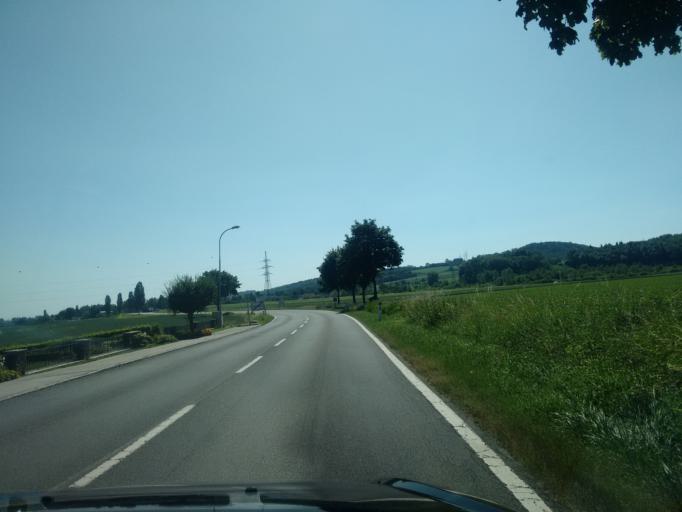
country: AT
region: Lower Austria
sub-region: Politischer Bezirk Tulln
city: Wurmla
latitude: 48.2761
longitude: 15.8721
